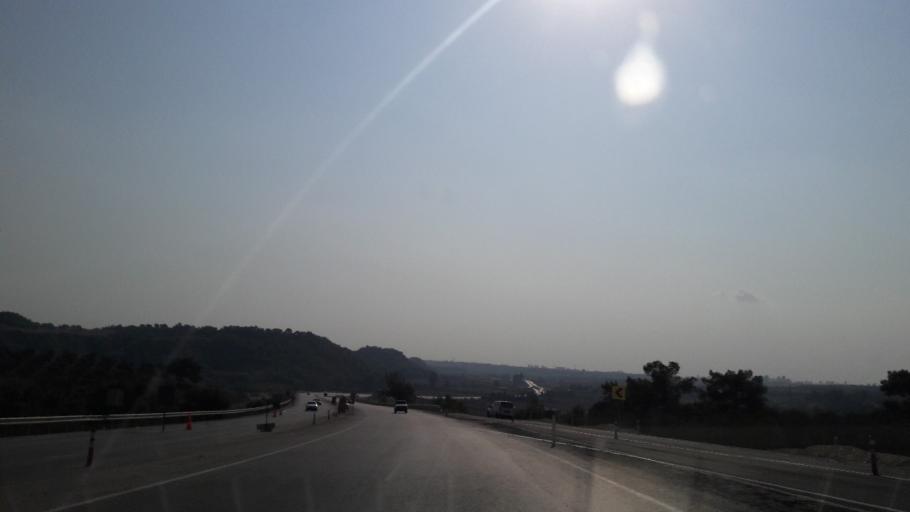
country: TR
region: Adana
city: Yuregir
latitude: 37.0800
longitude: 35.4744
